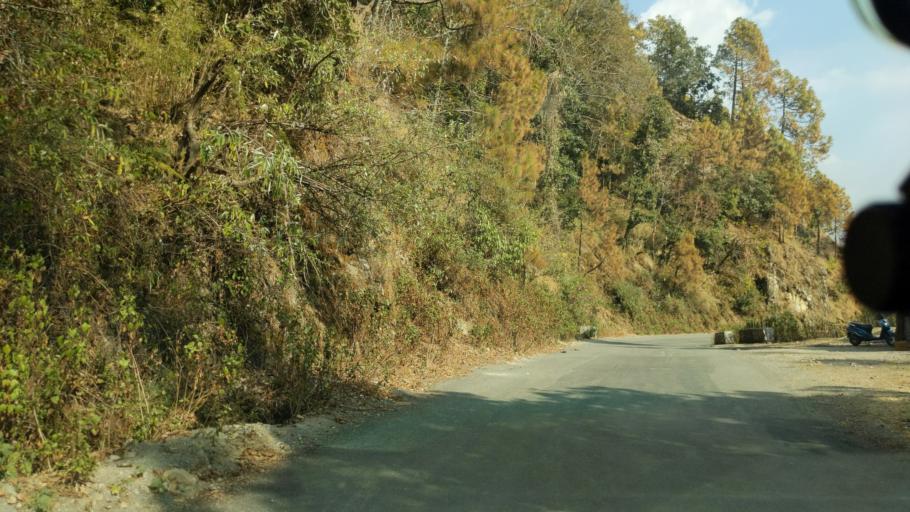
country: IN
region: Uttarakhand
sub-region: Naini Tal
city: Bhowali
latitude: 29.4025
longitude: 79.5349
